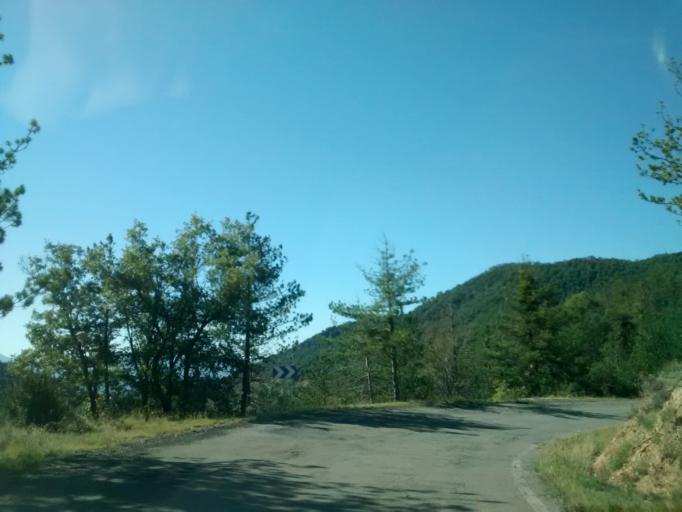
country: ES
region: Aragon
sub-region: Provincia de Huesca
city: Jaca
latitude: 42.4939
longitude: -0.5593
